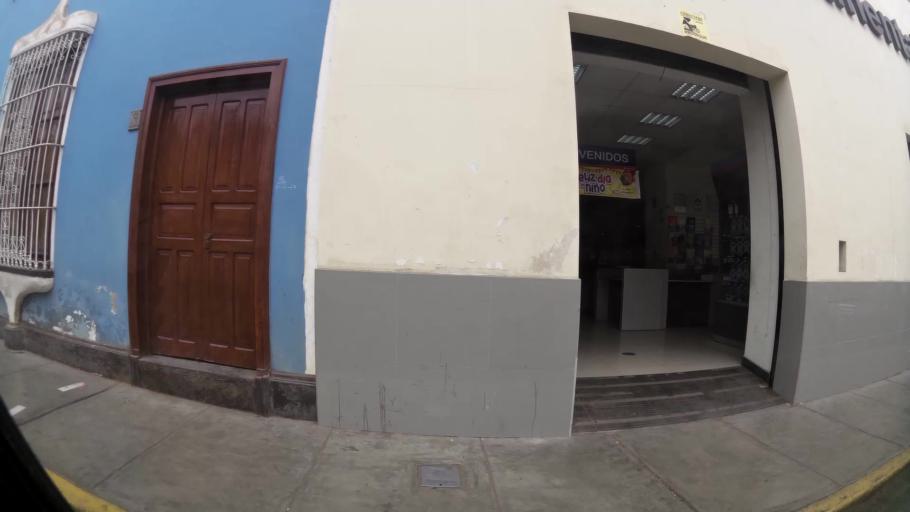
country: PE
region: La Libertad
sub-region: Provincia de Trujillo
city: Trujillo
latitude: -8.1136
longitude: -79.0264
